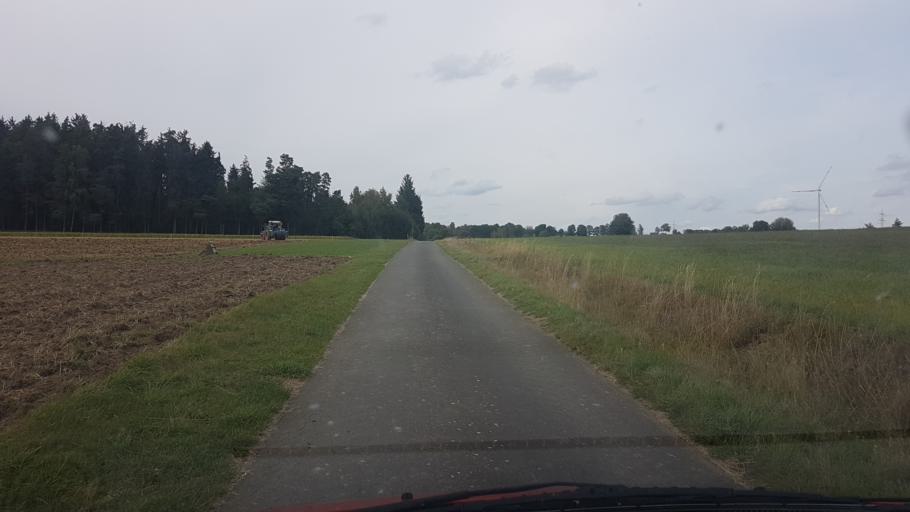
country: DE
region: Bavaria
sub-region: Upper Franconia
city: Hochstadt bei Thiersheim
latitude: 50.0717
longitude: 12.0686
